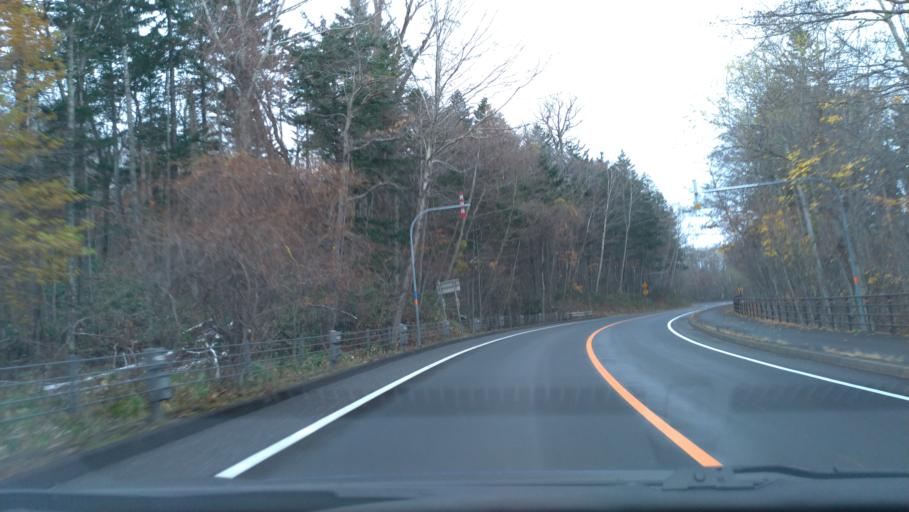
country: JP
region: Hokkaido
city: Shiraoi
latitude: 42.7344
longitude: 141.3743
